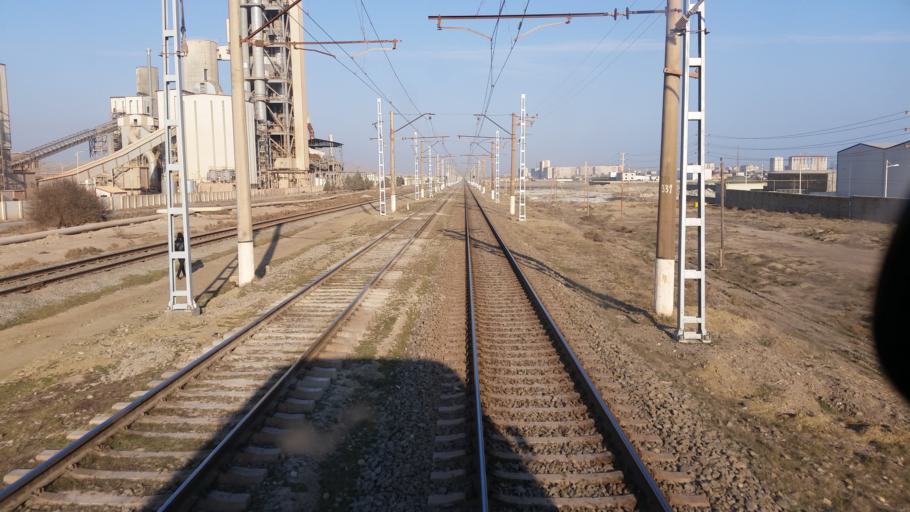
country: AZ
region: Baki
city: Korgoz
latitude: 40.2195
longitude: 49.5530
